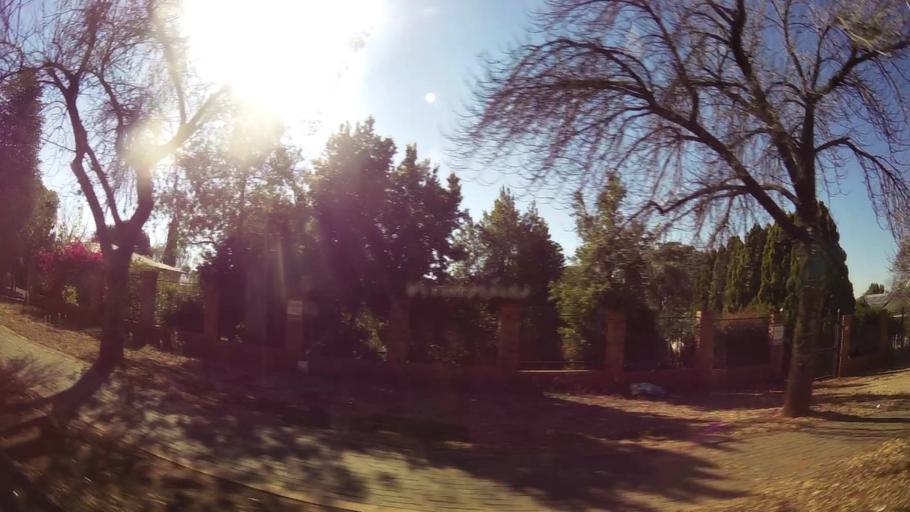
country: ZA
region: Gauteng
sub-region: City of Tshwane Metropolitan Municipality
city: Centurion
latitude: -25.8391
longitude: 28.2038
